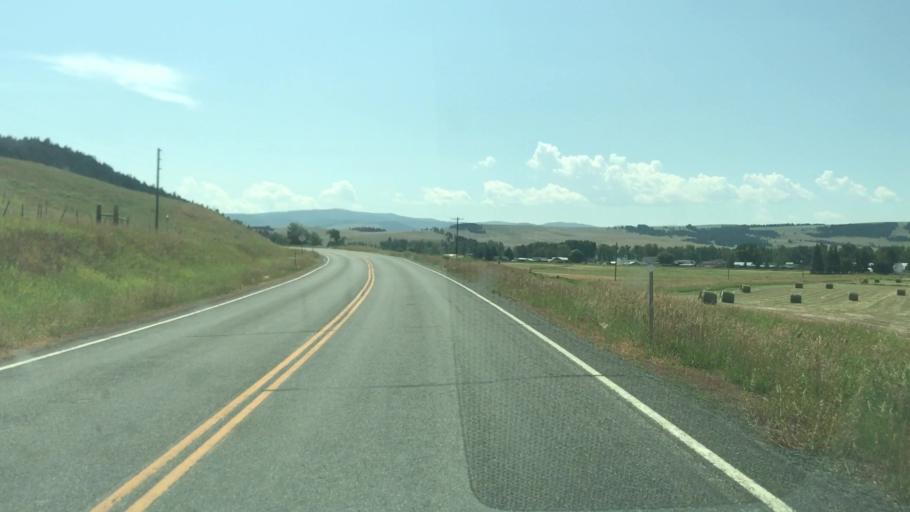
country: US
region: Montana
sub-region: Powell County
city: Deer Lodge
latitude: 46.6047
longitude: -112.5997
